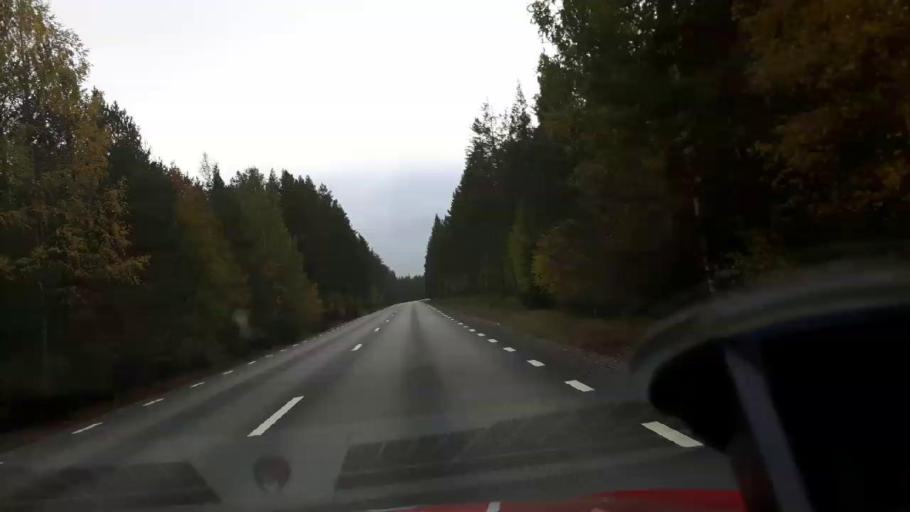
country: SE
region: Gaevleborg
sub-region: Ljusdals Kommun
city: Farila
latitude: 61.8548
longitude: 15.7474
